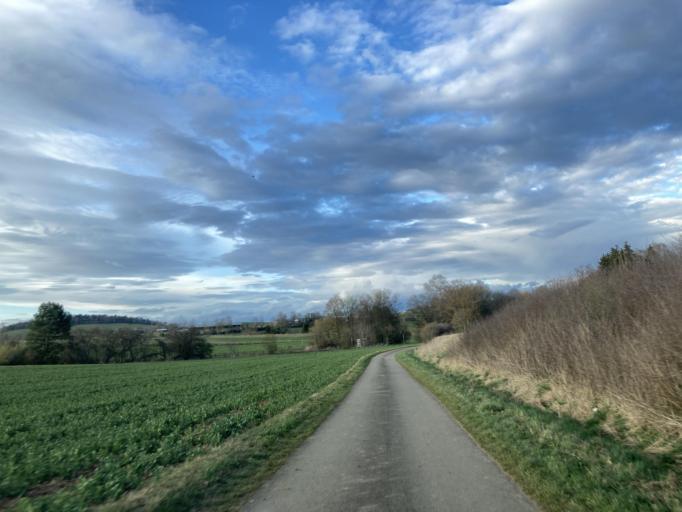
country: DE
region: Baden-Wuerttemberg
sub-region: Tuebingen Region
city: Rottenburg
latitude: 48.4810
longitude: 8.9082
